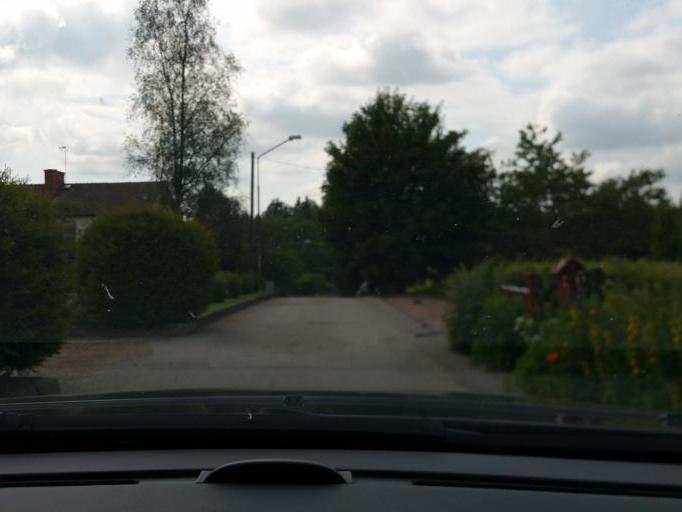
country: SE
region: Kronoberg
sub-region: Vaxjo Kommun
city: Lammhult
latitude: 57.1752
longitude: 14.5874
